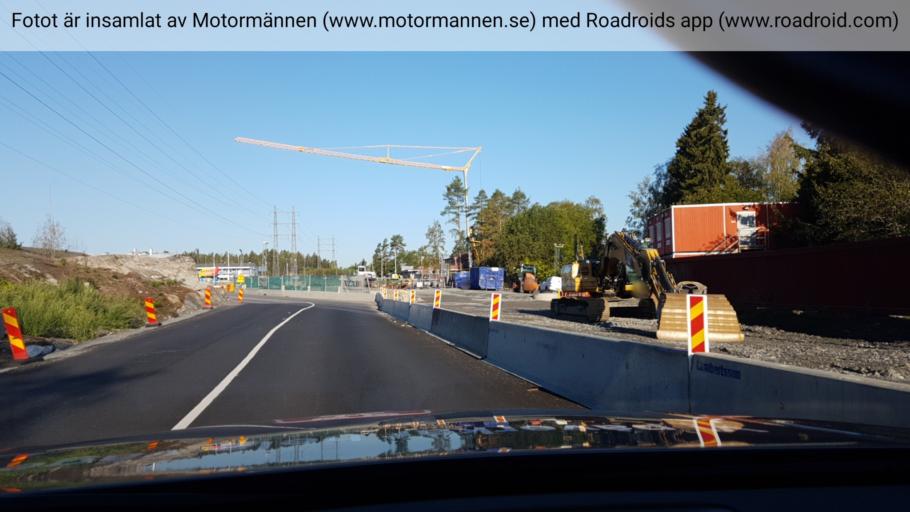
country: SE
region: Stockholm
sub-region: Tyreso Kommun
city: Bollmora
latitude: 59.2471
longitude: 18.2515
